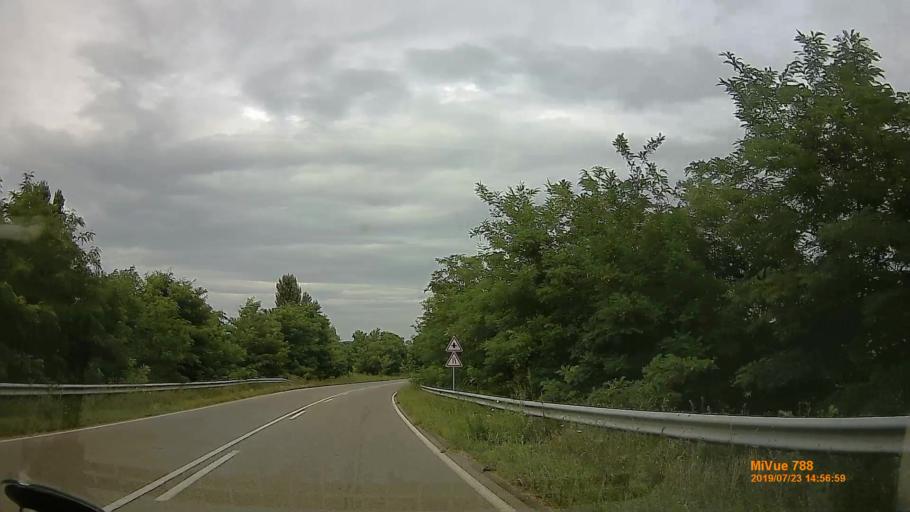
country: HU
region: Szabolcs-Szatmar-Bereg
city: Nyiregyhaza
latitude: 47.9026
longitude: 21.6681
